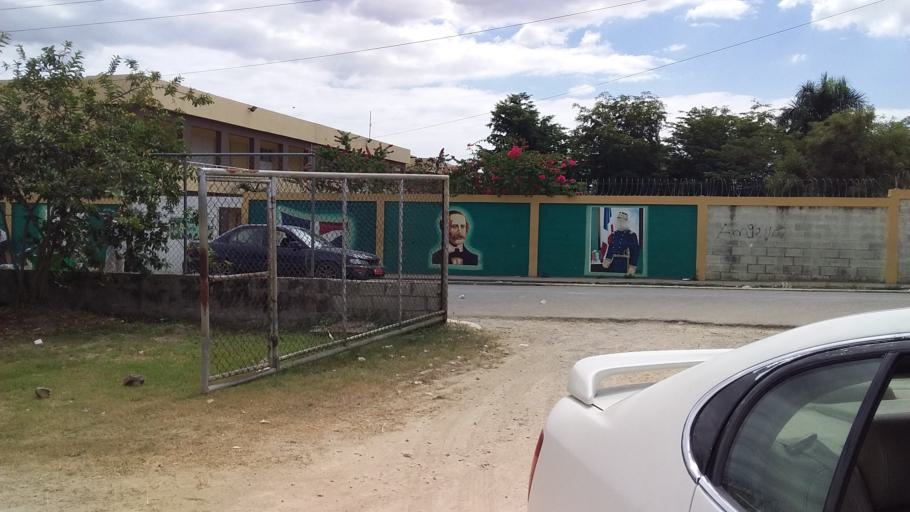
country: DO
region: Santo Domingo
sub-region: Santo Domingo
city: Santo Domingo Este
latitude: 18.5459
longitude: -69.7934
